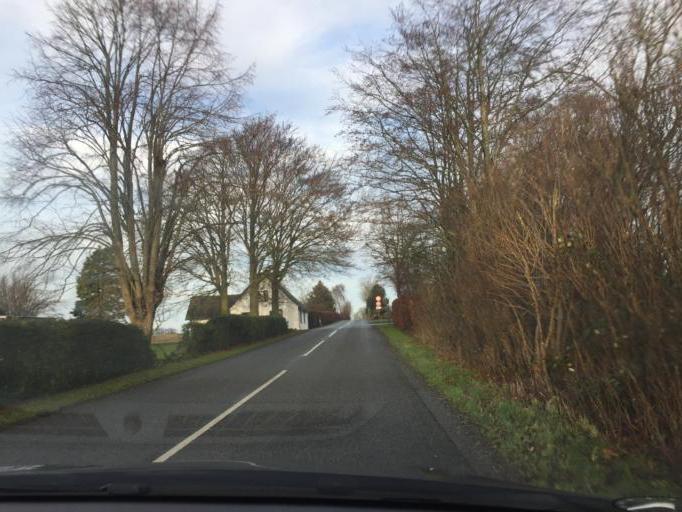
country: DK
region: South Denmark
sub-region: Faaborg-Midtfyn Kommune
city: Ringe
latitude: 55.1753
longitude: 10.4044
